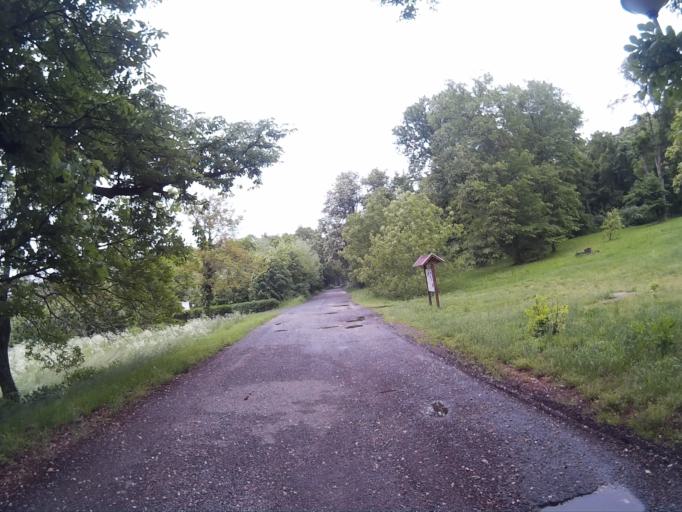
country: HU
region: Veszprem
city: Sumeg
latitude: 46.9343
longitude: 17.2933
